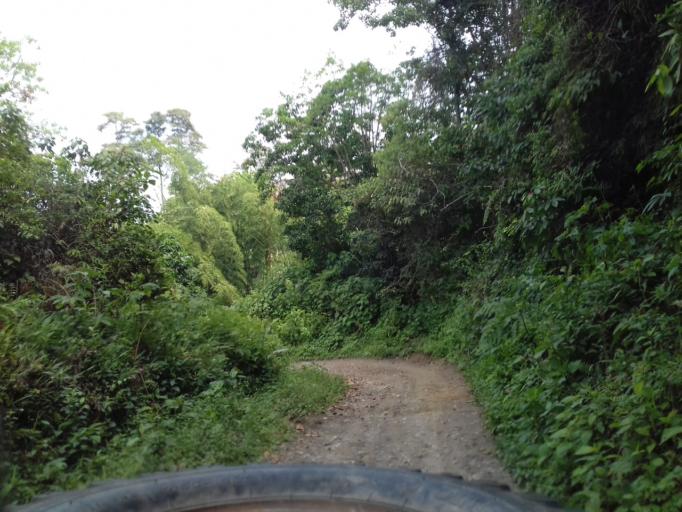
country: CO
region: Tolima
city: Libano
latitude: 4.9288
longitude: -75.0864
